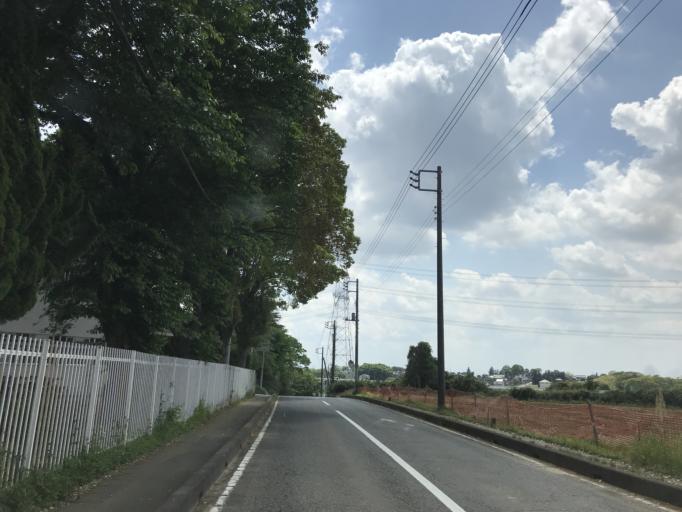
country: JP
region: Ibaraki
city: Mitsukaido
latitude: 36.0636
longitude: 140.0407
